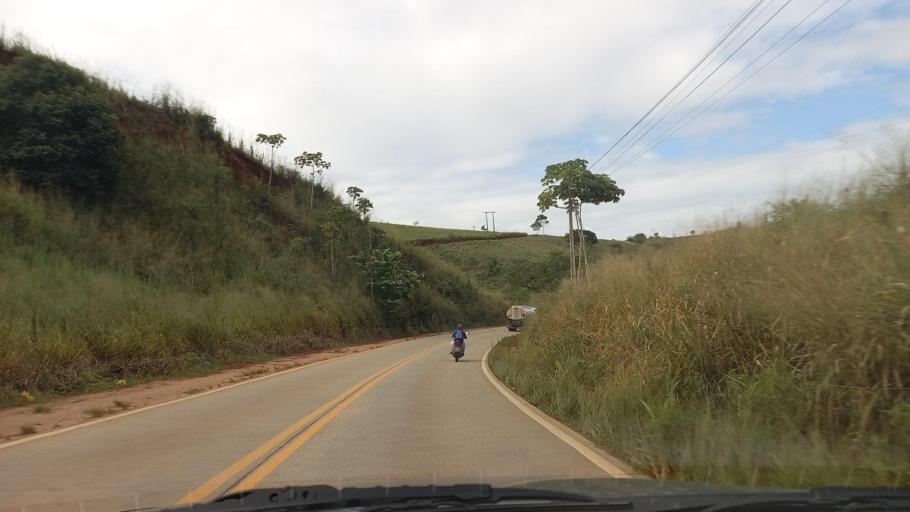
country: BR
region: Pernambuco
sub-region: Maraial
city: Maraial
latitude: -8.7469
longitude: -35.8053
